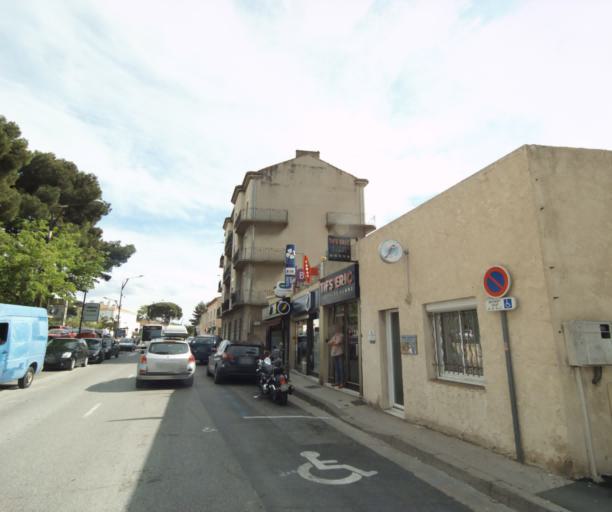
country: FR
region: Provence-Alpes-Cote d'Azur
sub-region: Departement des Bouches-du-Rhone
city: Rognac
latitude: 43.4877
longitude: 5.2301
